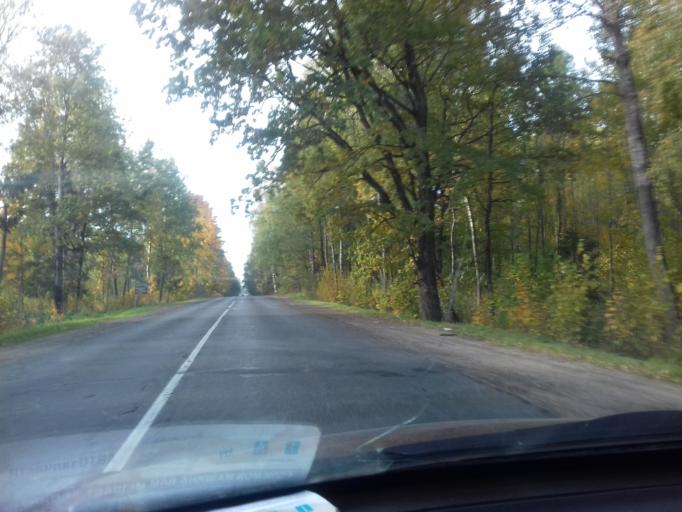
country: BY
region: Minsk
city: Hatava
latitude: 53.7585
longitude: 27.6538
